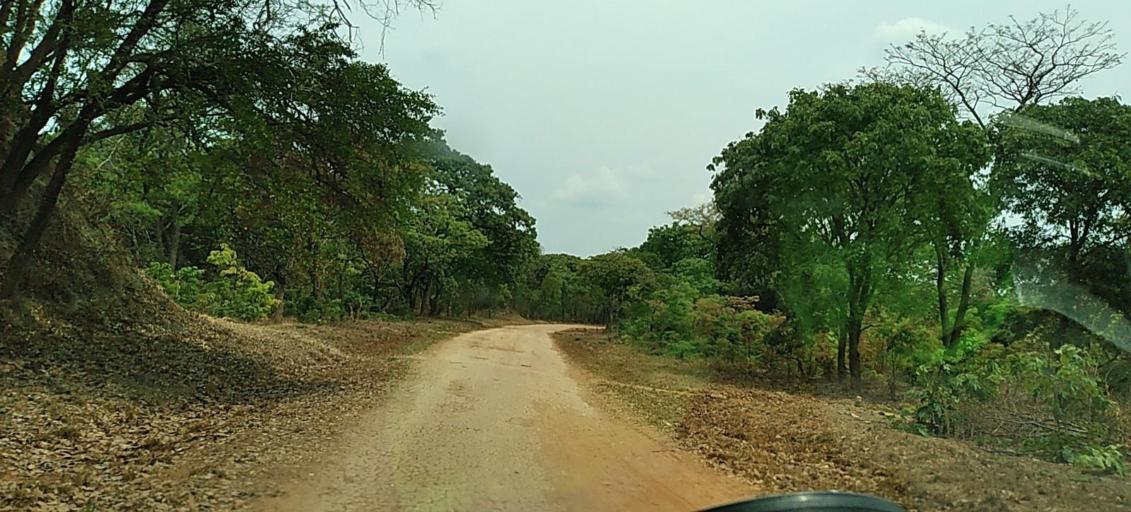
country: ZM
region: North-Western
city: Solwezi
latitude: -12.8255
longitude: 26.5375
